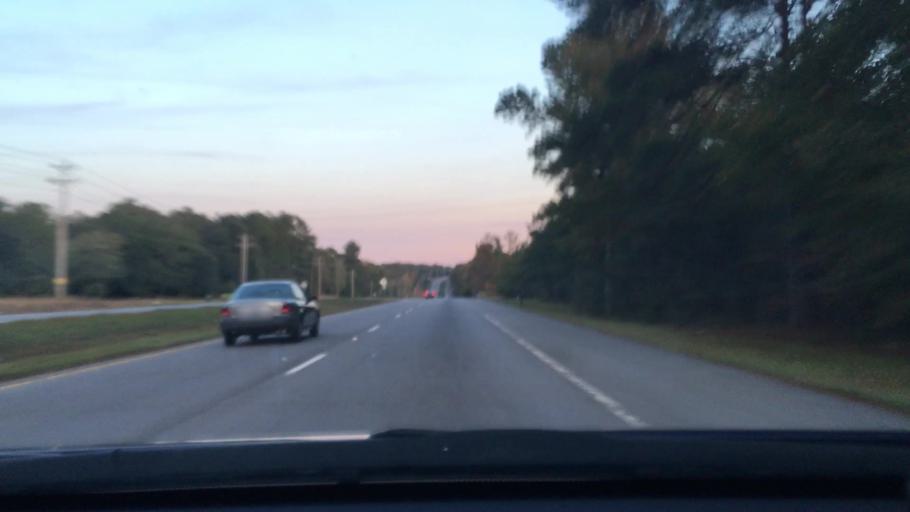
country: US
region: South Carolina
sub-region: Richland County
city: Gadsden
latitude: 33.9434
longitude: -80.7383
